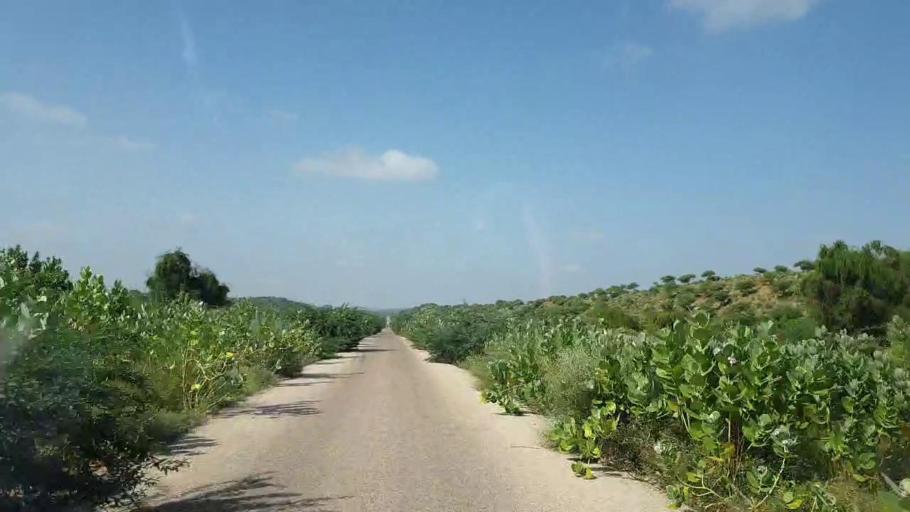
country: PK
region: Sindh
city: Mithi
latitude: 24.5446
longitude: 69.8744
